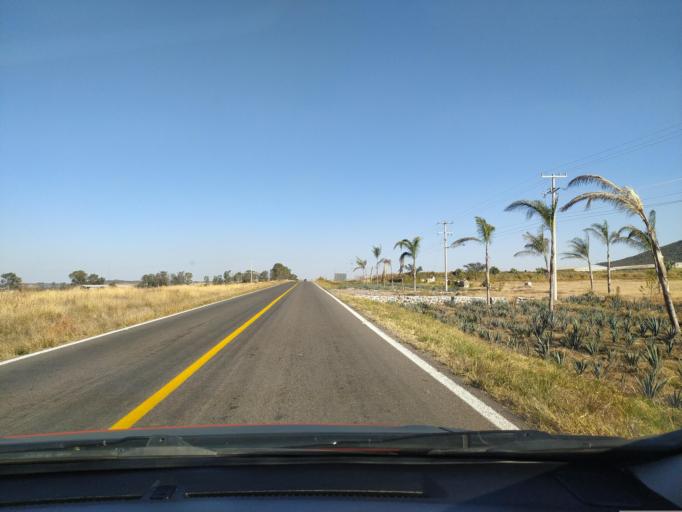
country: MX
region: Jalisco
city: San Miguel el Alto
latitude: 21.0169
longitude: -102.4701
